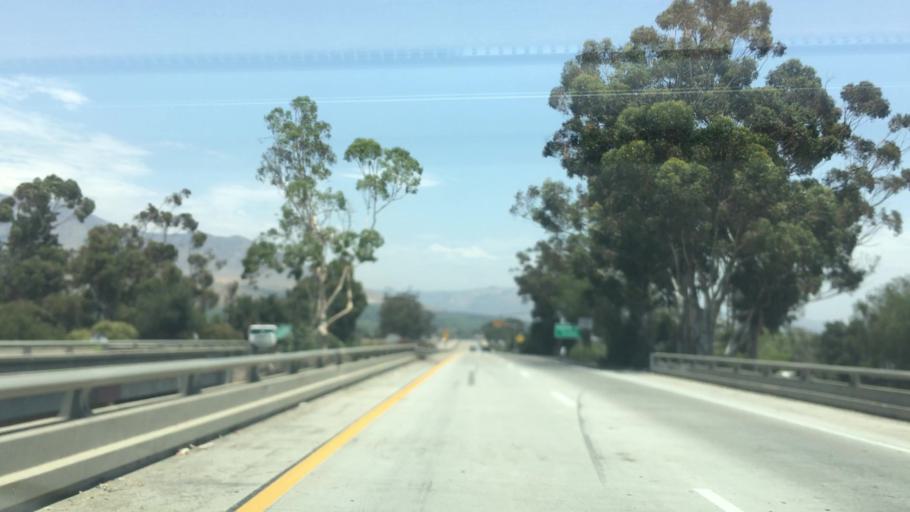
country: US
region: California
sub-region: Ventura County
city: Santa Paula
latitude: 34.3550
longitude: -119.0483
